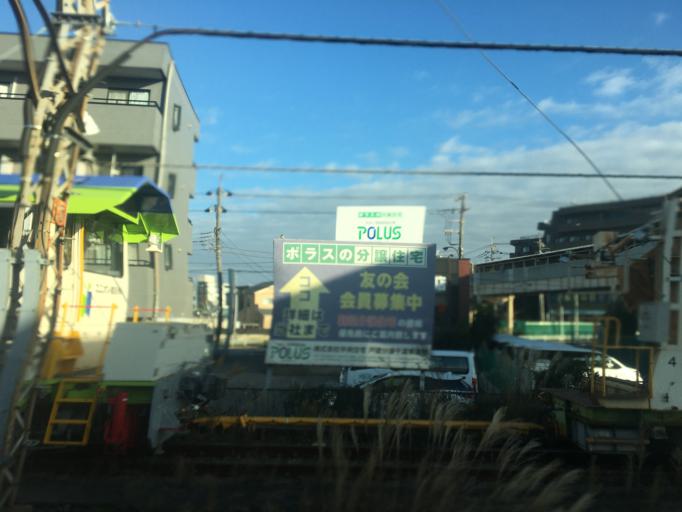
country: JP
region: Chiba
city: Kashiwa
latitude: 35.8760
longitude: 139.9878
